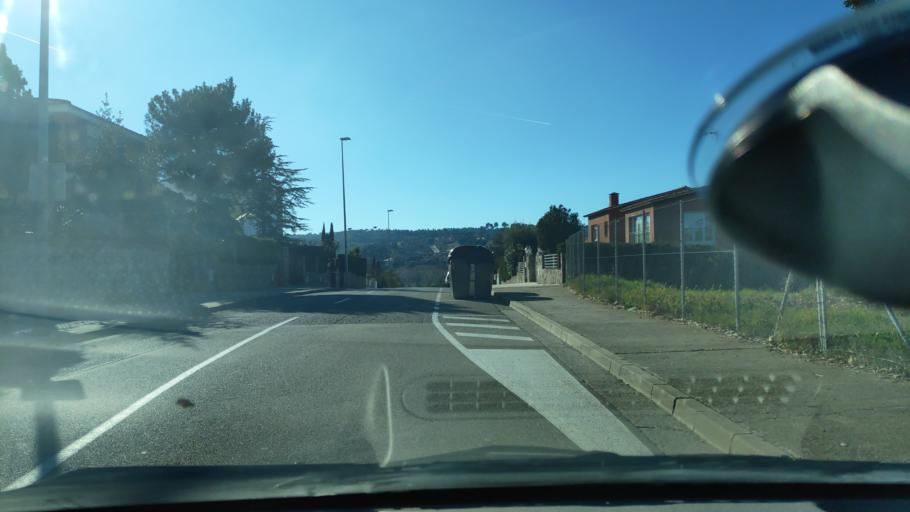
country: ES
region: Catalonia
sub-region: Provincia de Barcelona
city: Sant Quirze del Valles
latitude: 41.5415
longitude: 2.0656
